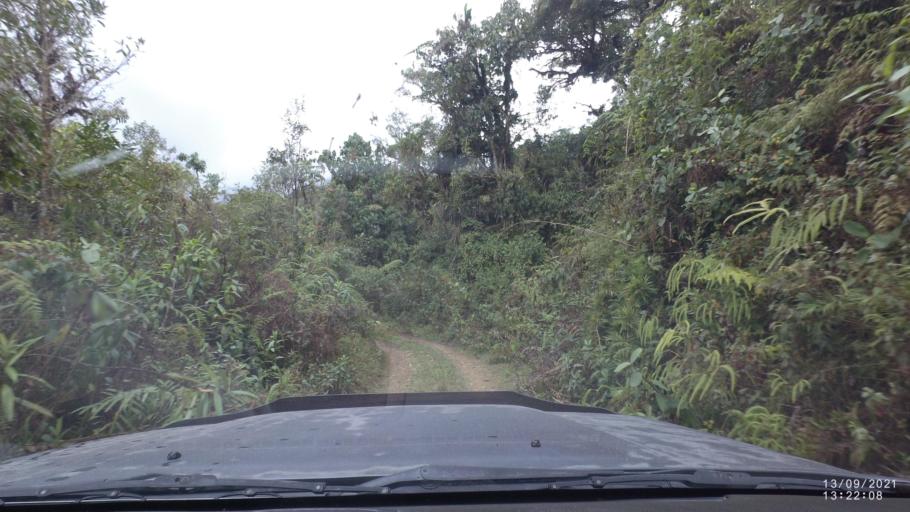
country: BO
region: Cochabamba
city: Colomi
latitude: -17.2079
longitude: -65.8624
